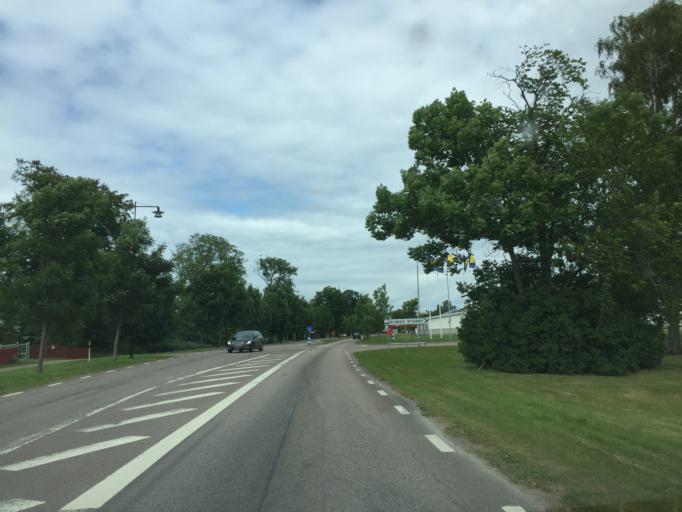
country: SE
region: OEstergoetland
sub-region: Vadstena Kommun
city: Vadstena
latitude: 58.4398
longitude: 14.8797
